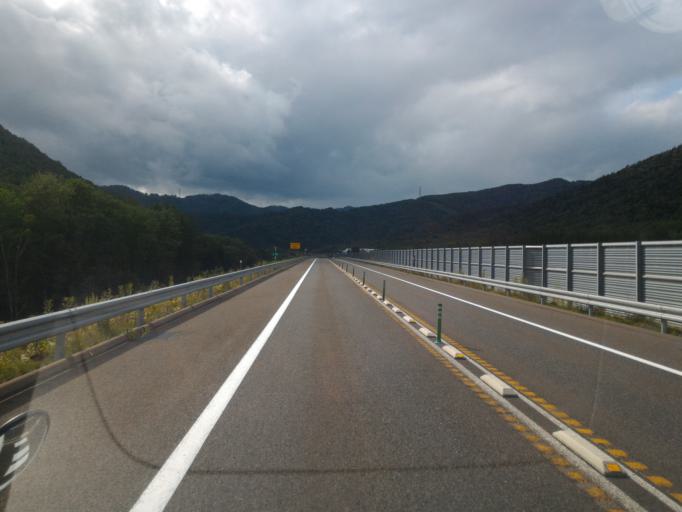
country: JP
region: Hokkaido
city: Shimo-furano
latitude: 43.0623
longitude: 142.5509
